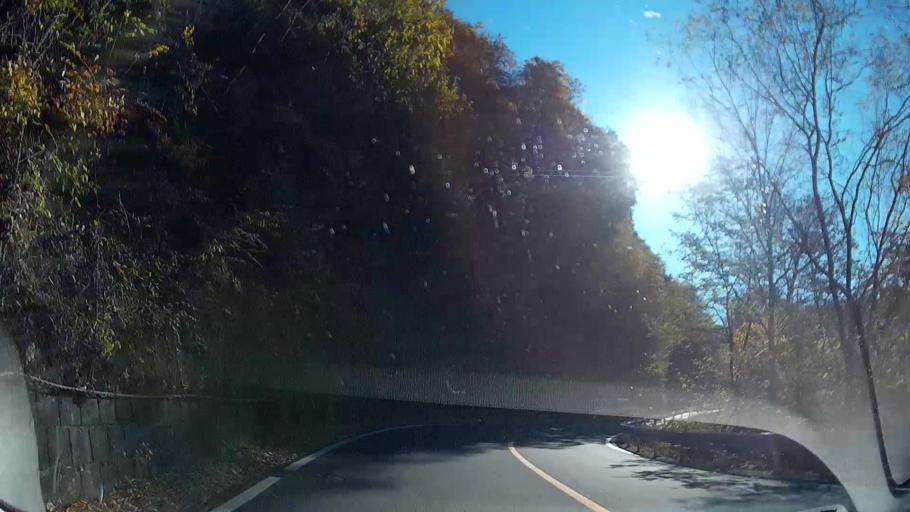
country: JP
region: Nagano
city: Toyoshina
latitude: 36.1440
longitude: 137.7423
